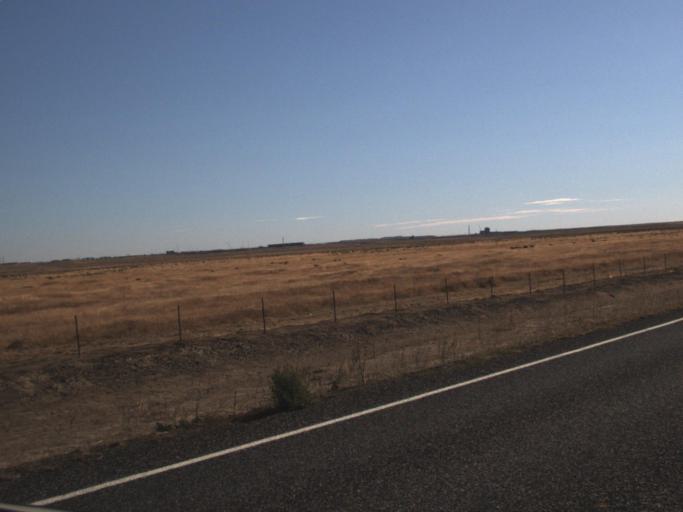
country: US
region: Washington
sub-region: Grant County
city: Desert Aire
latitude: 46.5539
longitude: -119.6998
